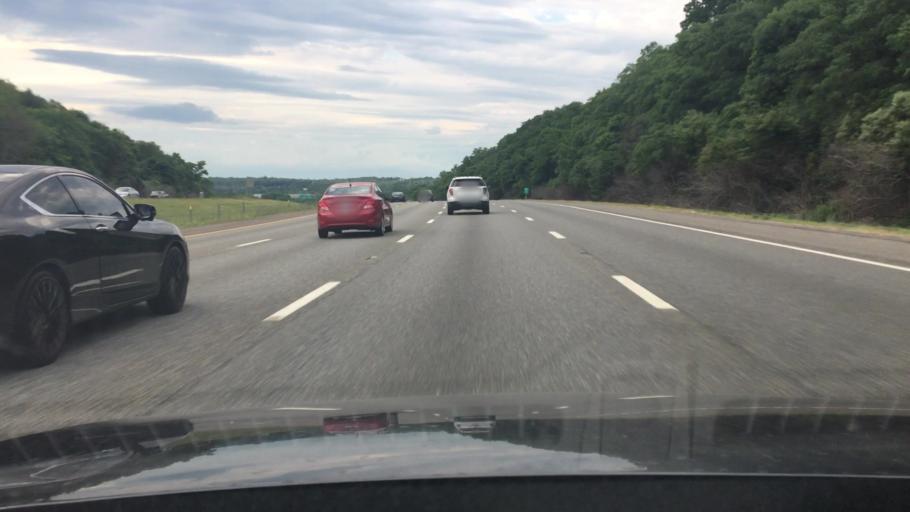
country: US
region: Massachusetts
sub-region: Essex County
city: Danvers
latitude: 42.5863
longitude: -70.9611
